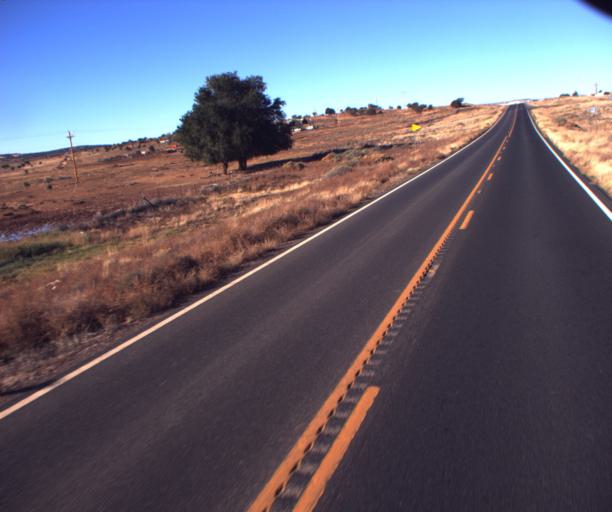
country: US
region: Arizona
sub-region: Apache County
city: Ganado
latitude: 35.7848
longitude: -109.7059
